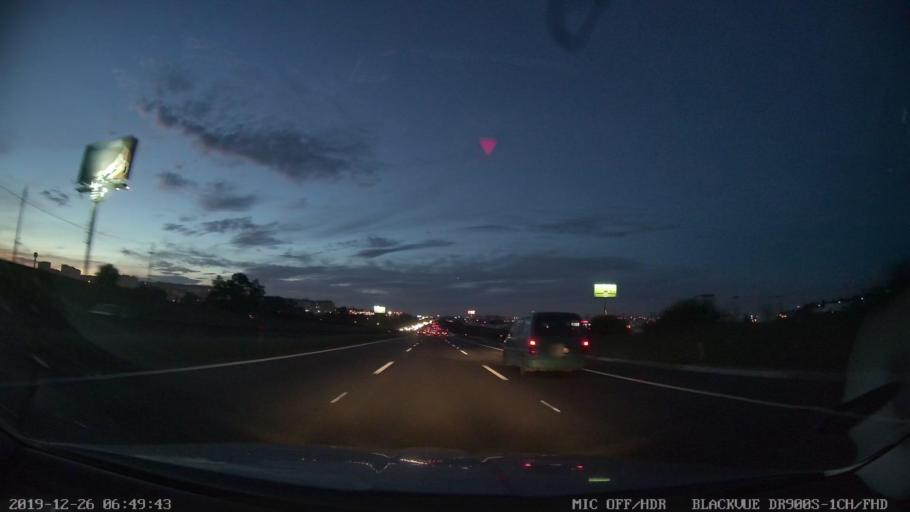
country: PT
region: Setubal
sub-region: Seixal
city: Corroios
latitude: 38.6288
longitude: -9.1421
